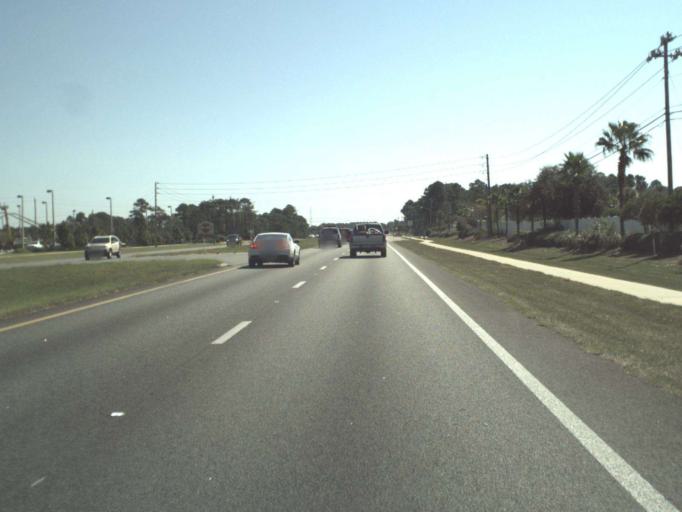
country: US
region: Florida
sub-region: Bay County
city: Panama City Beach
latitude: 30.2148
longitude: -85.8564
